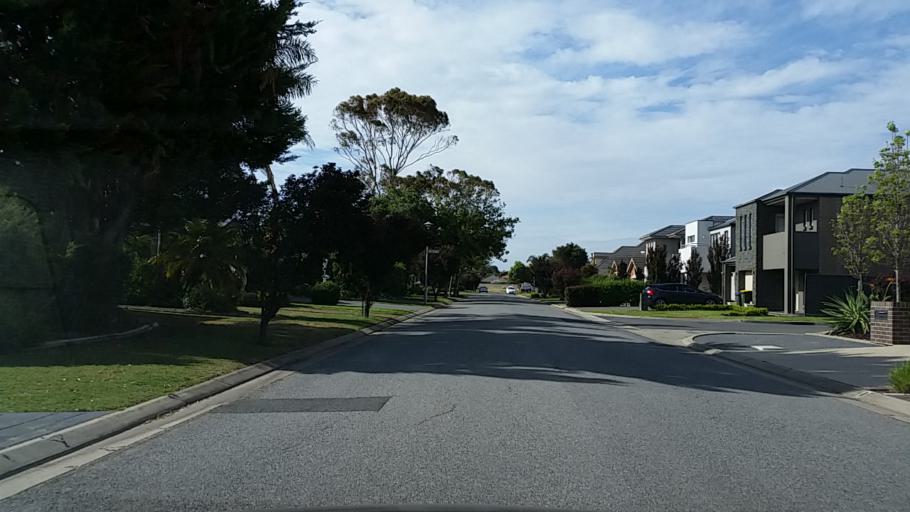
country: AU
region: South Australia
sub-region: Charles Sturt
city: Grange
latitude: -34.8944
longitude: 138.4993
